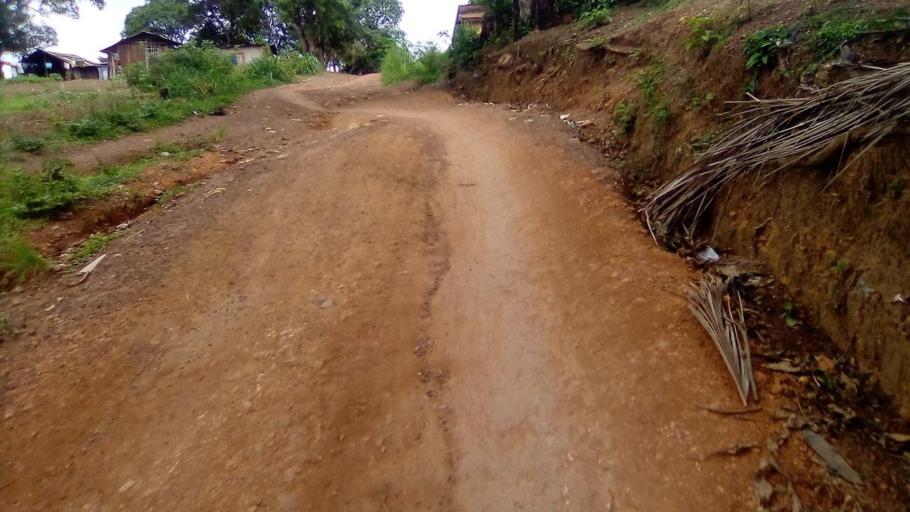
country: SL
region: Southern Province
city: Bo
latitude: 7.9619
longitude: -11.7236
